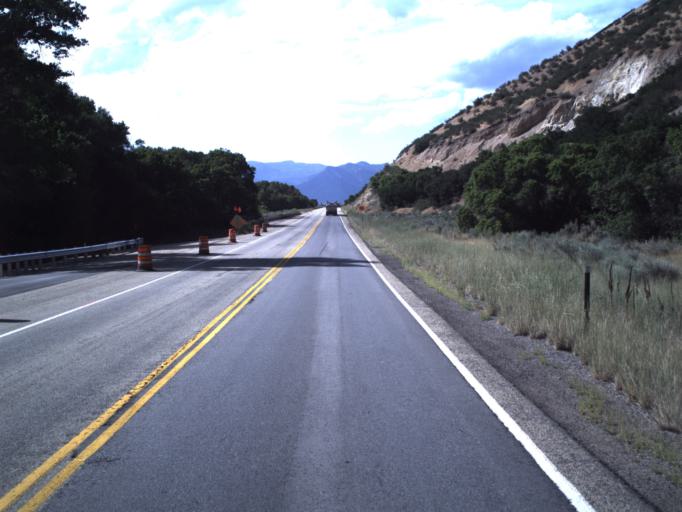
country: US
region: Utah
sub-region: Wasatch County
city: Heber
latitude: 40.4305
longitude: -111.3514
